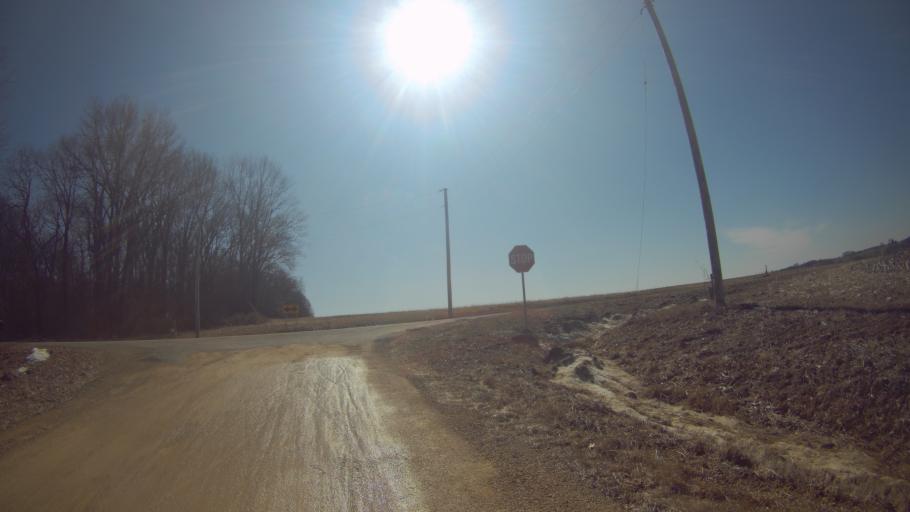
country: US
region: Illinois
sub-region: Winnebago County
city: Pecatonica
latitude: 42.3468
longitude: -89.4076
